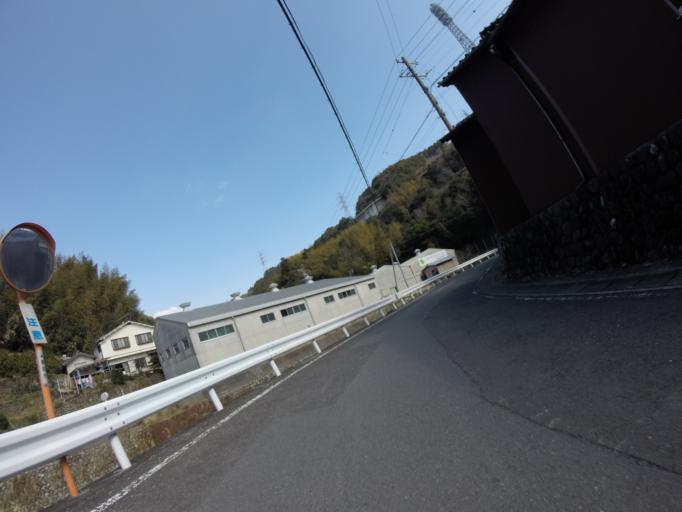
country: JP
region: Shizuoka
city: Shizuoka-shi
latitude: 35.0574
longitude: 138.4974
